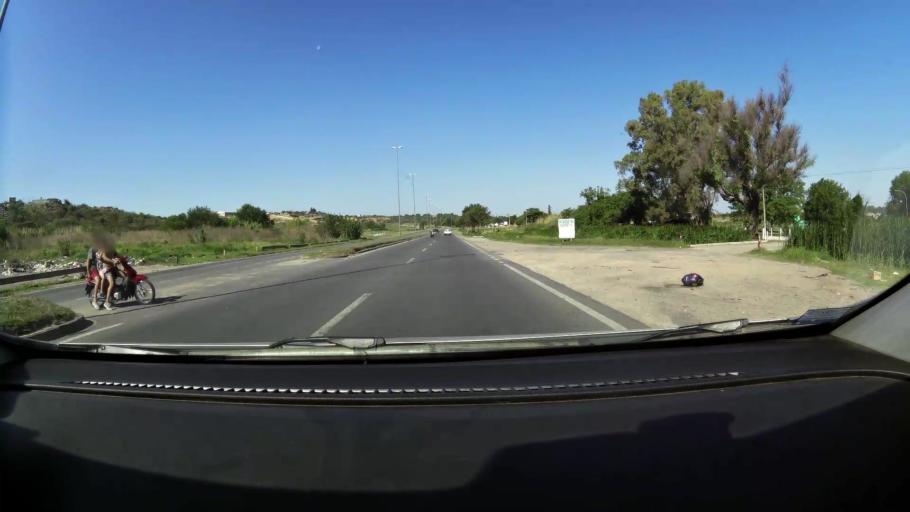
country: AR
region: Cordoba
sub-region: Departamento de Capital
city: Cordoba
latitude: -31.4005
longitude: -64.1469
